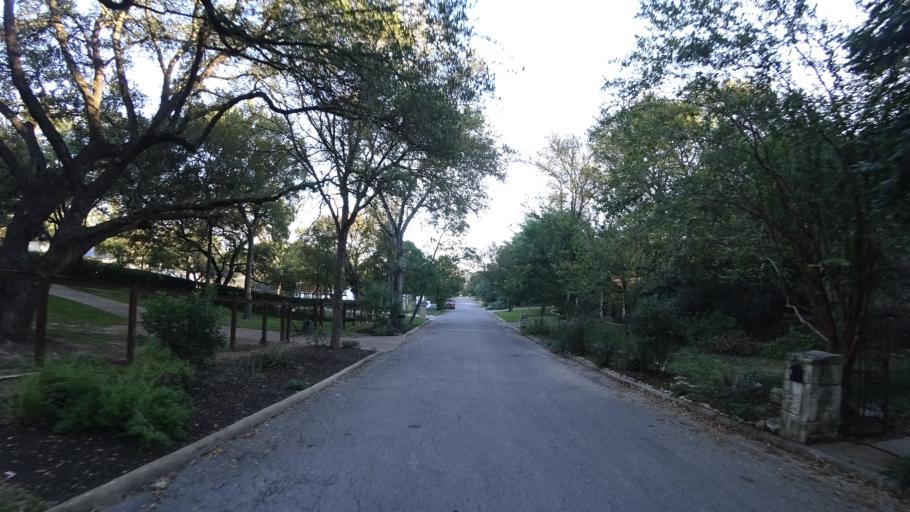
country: US
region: Texas
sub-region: Travis County
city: West Lake Hills
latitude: 30.3451
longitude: -97.8089
